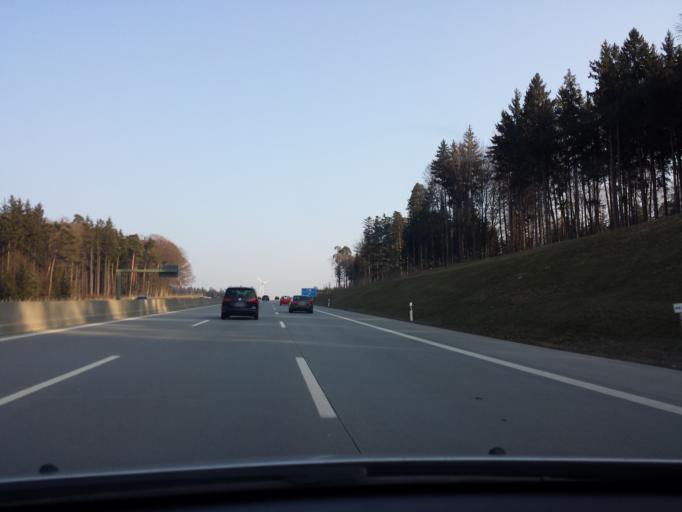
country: DE
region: Bavaria
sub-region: Swabia
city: Adelzhausen
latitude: 48.3459
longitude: 11.1435
